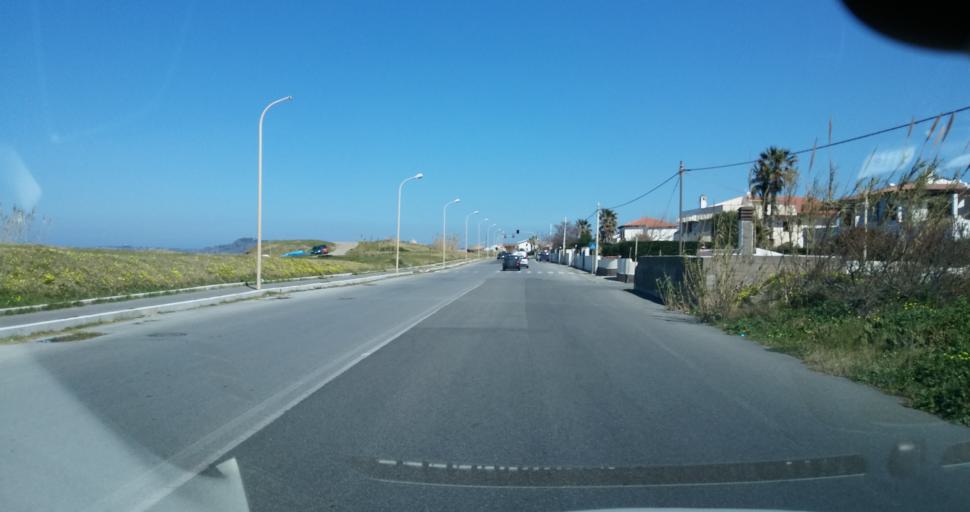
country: IT
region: Sicily
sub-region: Messina
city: Milazzo
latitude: 38.1922
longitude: 15.2179
